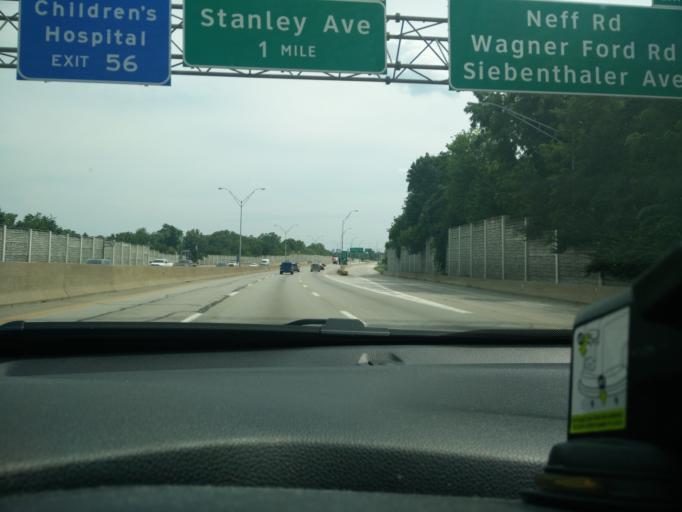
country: US
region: Ohio
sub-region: Montgomery County
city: Northridge
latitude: 39.8060
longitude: -84.1890
